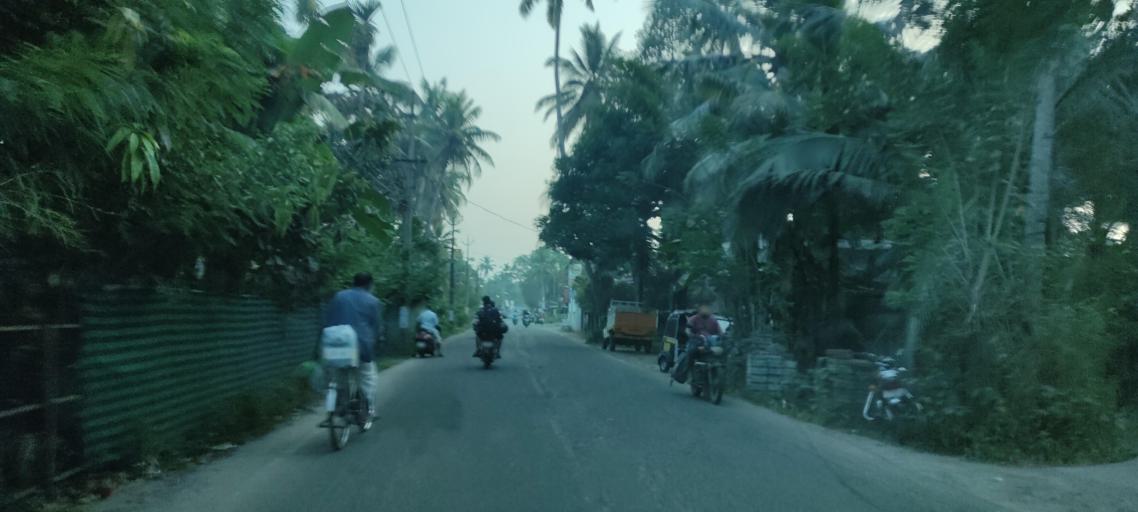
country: IN
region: Kerala
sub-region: Alappuzha
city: Kayankulam
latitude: 9.1275
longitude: 76.5028
